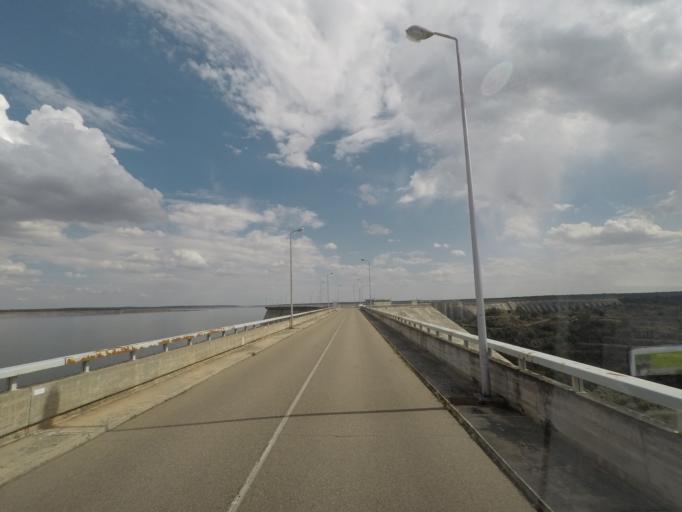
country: ES
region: Castille and Leon
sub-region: Provincia de Salamanca
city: Almendra
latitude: 41.2742
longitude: -6.3245
